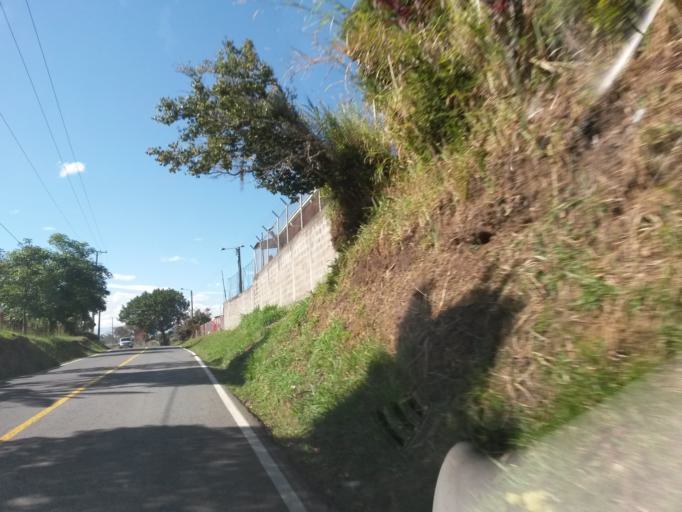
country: CO
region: Cauca
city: Morales
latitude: 2.7473
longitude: -76.6230
